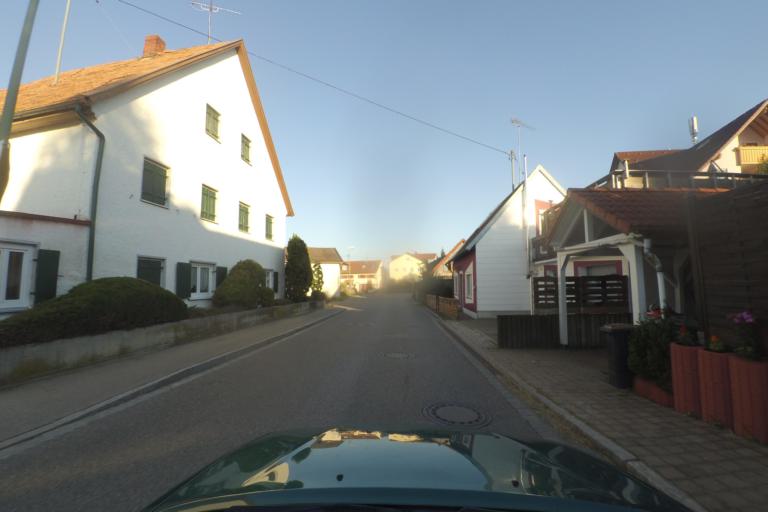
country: DE
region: Bavaria
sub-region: Upper Bavaria
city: Weil
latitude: 48.1190
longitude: 10.9240
